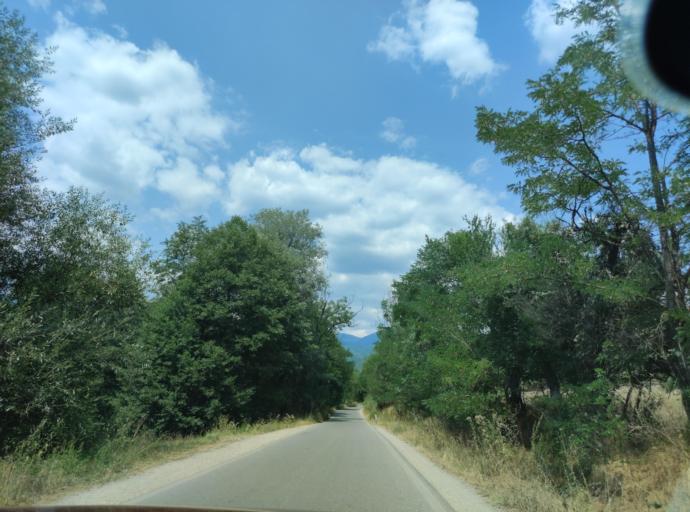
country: BG
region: Blagoevgrad
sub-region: Obshtina Belitsa
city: Belitsa
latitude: 41.9769
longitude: 23.5537
